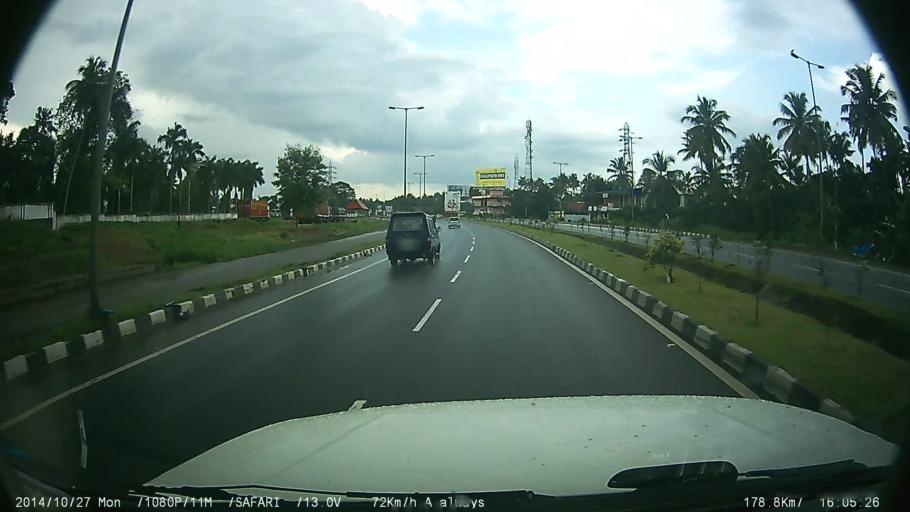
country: IN
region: Kerala
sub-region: Thrissur District
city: Kizhake Chalakudi
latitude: 10.3468
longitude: 76.3213
